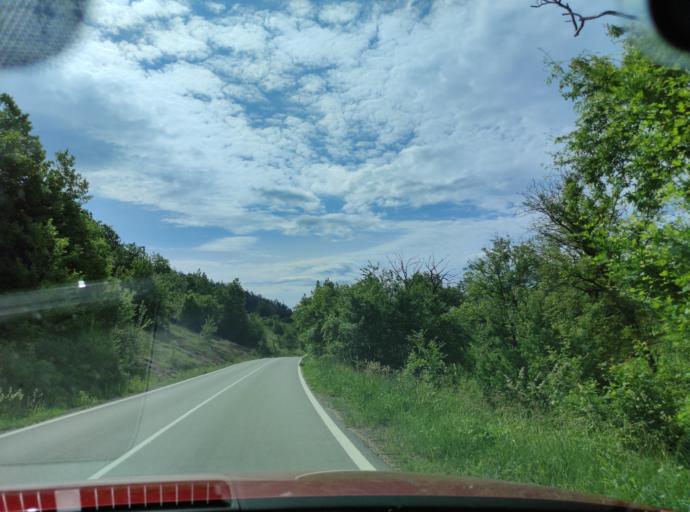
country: BG
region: Montana
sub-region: Obshtina Chiprovtsi
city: Chiprovtsi
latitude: 43.4555
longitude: 22.9026
